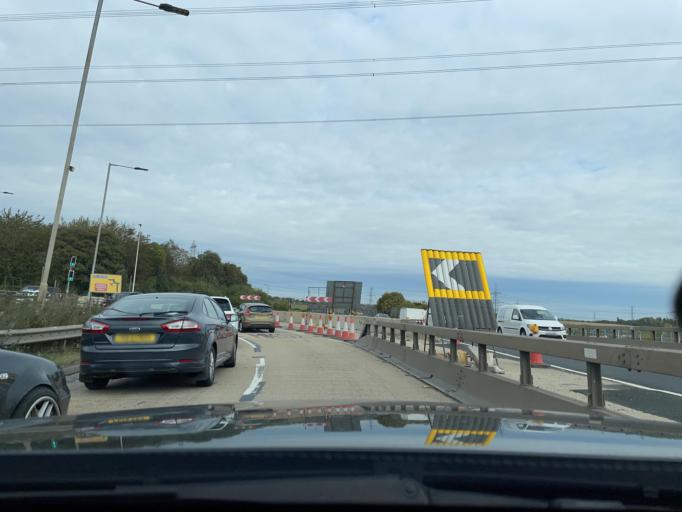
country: GB
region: England
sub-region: Rotherham
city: Treeton
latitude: 53.3970
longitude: -1.3502
